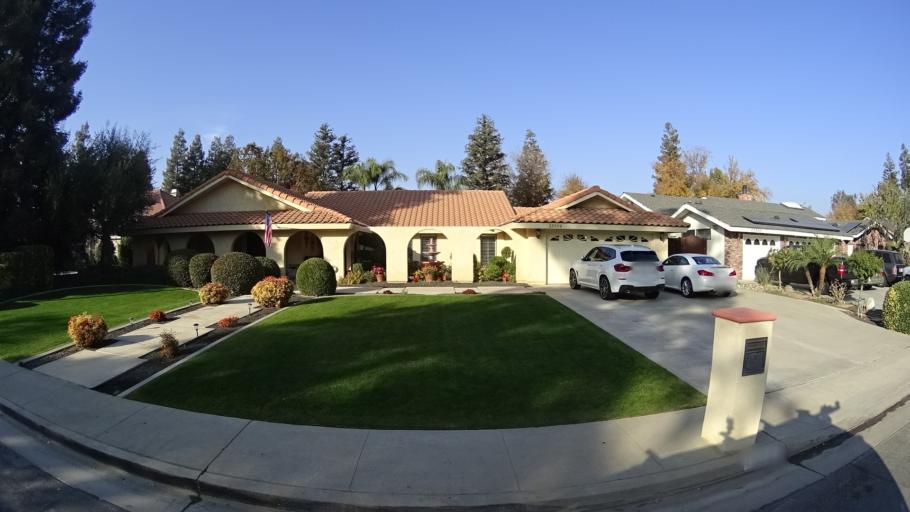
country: US
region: California
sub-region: Kern County
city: Rosedale
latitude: 35.3566
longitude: -119.1503
